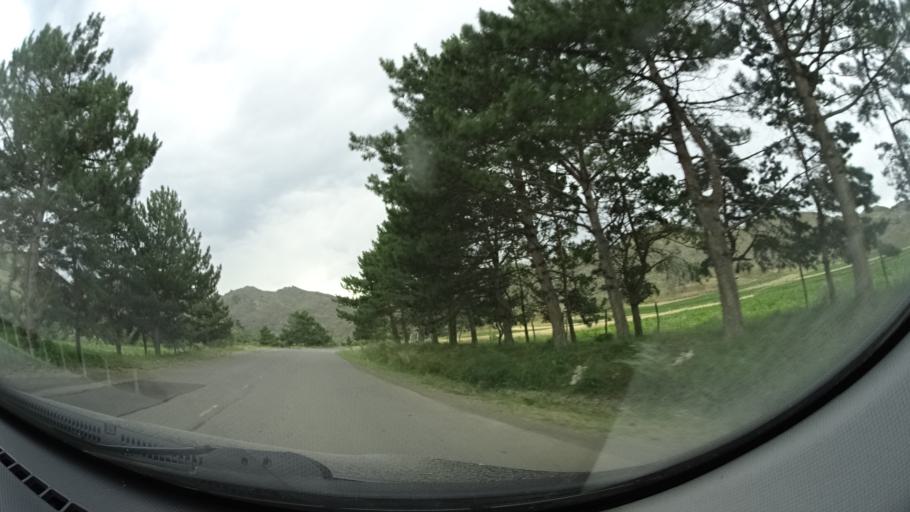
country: GE
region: Samtskhe-Javakheti
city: Aspindza
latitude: 41.6154
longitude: 43.1189
